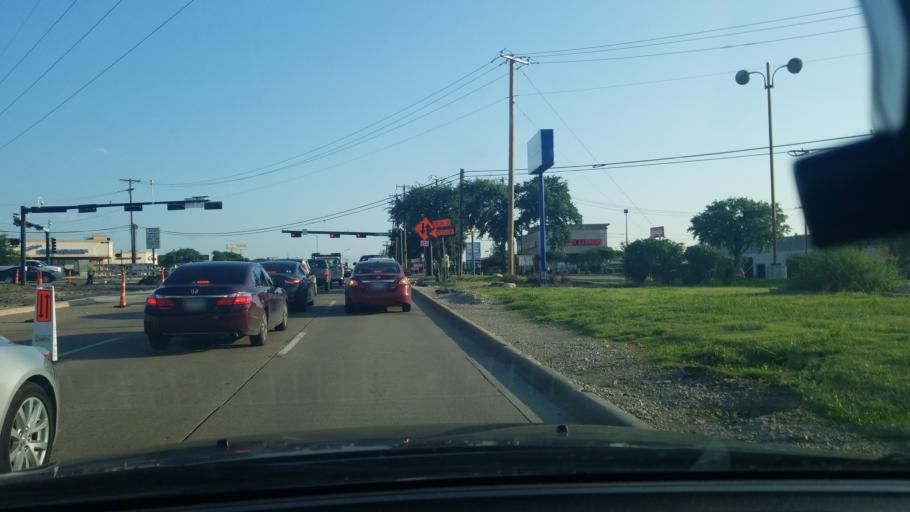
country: US
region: Texas
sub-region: Dallas County
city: Mesquite
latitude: 32.8106
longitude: -96.6344
